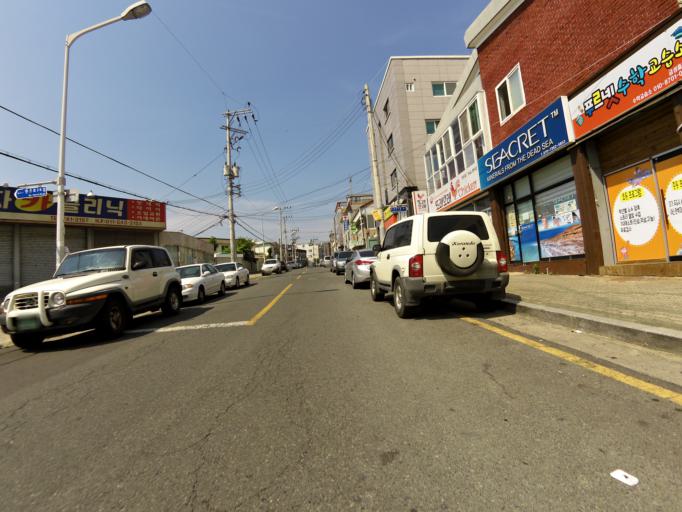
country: KR
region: Daegu
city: Daegu
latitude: 35.8702
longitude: 128.6424
